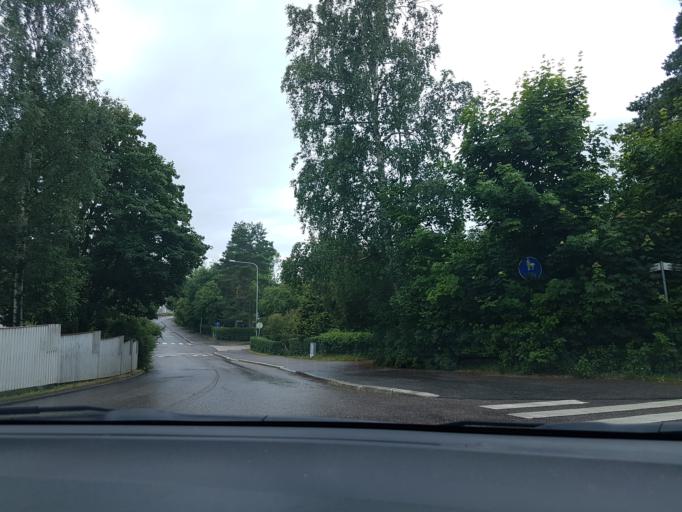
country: FI
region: Uusimaa
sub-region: Helsinki
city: Vantaa
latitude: 60.2203
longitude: 25.1050
